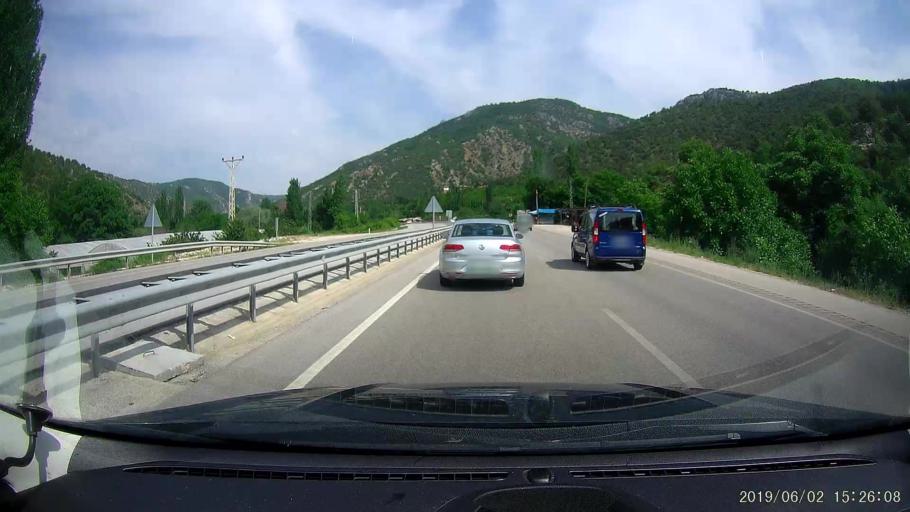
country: TR
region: Amasya
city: Saraycik
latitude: 40.9878
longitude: 35.0312
